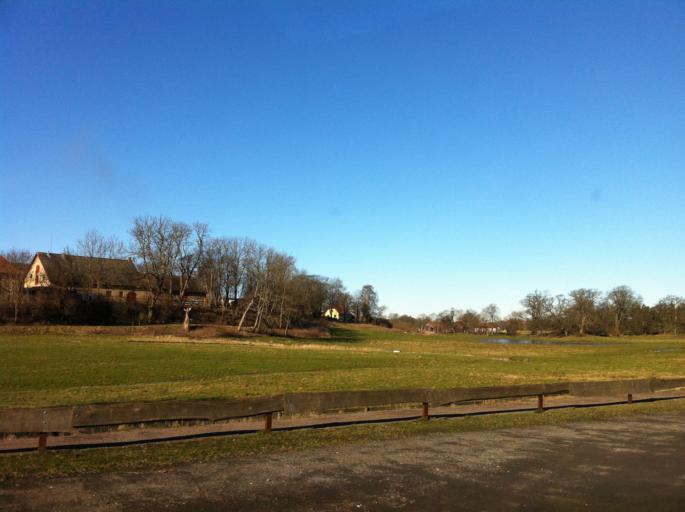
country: SE
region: Skane
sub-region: Svedala Kommun
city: Klagerup
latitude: 55.5690
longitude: 13.2317
